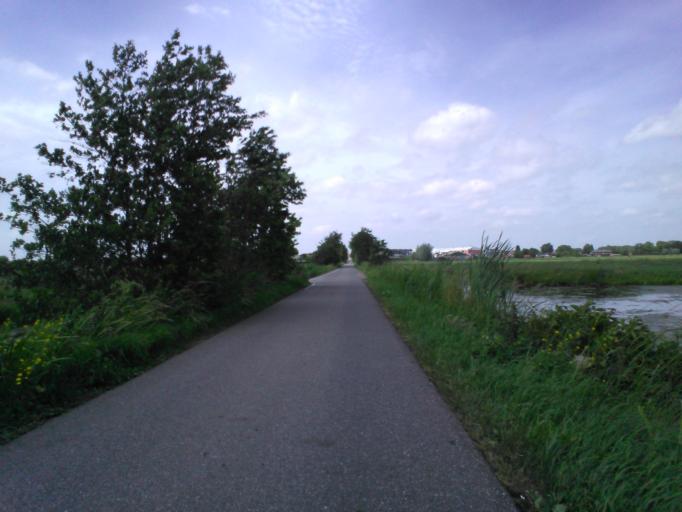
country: NL
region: South Holland
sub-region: Gemeente Gouda
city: Gouda
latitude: 51.9686
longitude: 4.6591
